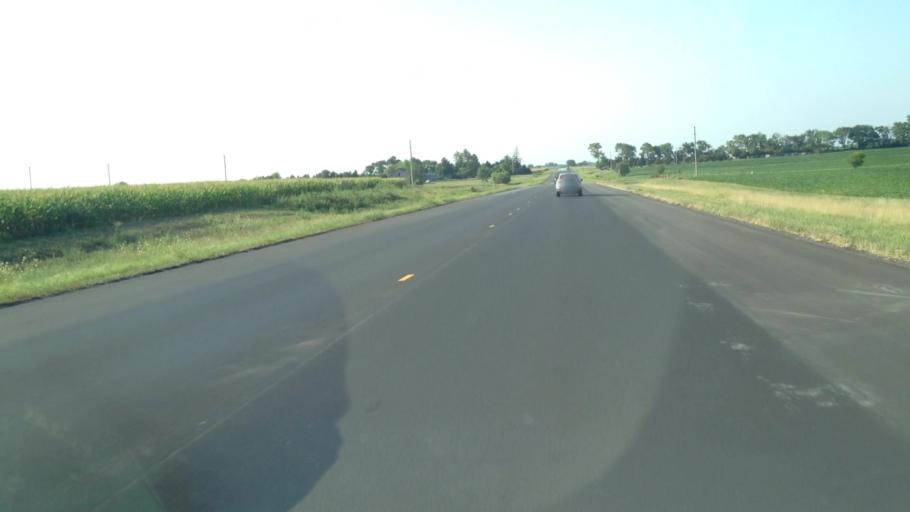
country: US
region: Kansas
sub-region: Anderson County
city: Garnett
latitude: 38.4464
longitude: -95.2488
